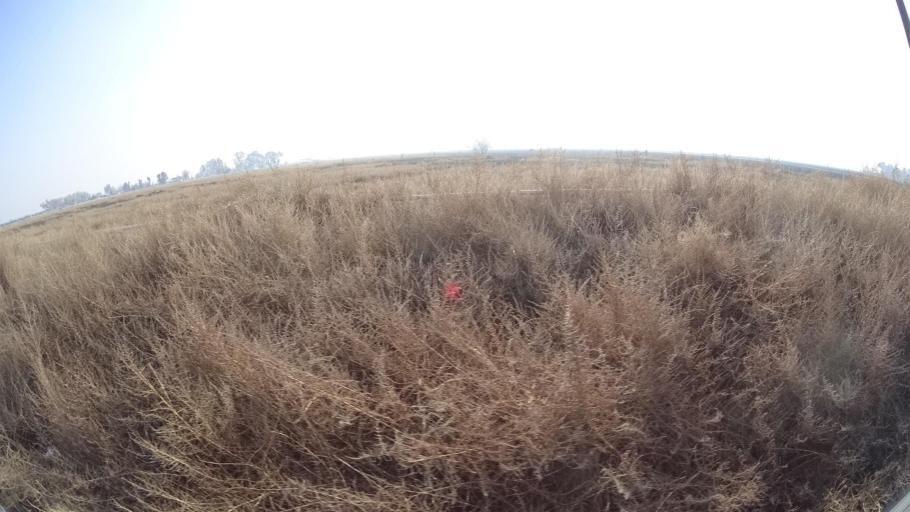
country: US
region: California
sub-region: Kern County
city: Greenfield
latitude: 35.1505
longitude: -119.0028
